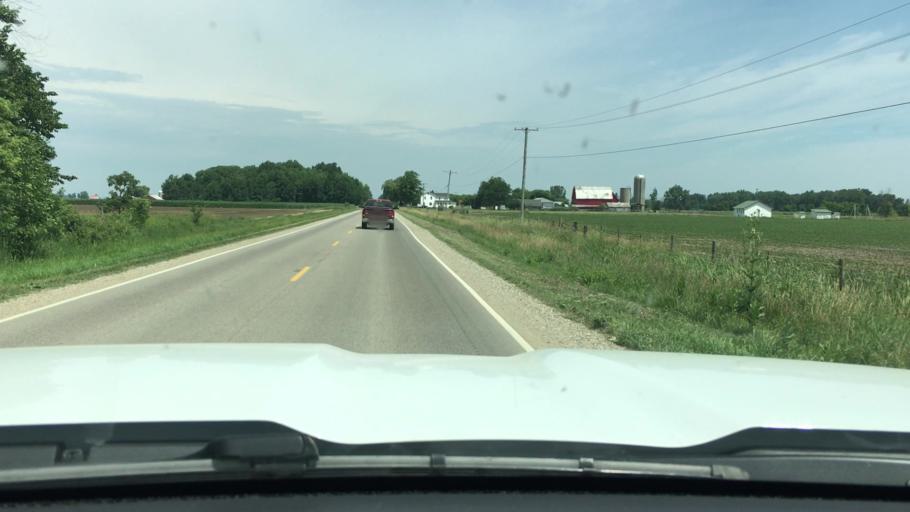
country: US
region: Michigan
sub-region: Sanilac County
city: Brown City
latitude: 43.2971
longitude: -82.9832
